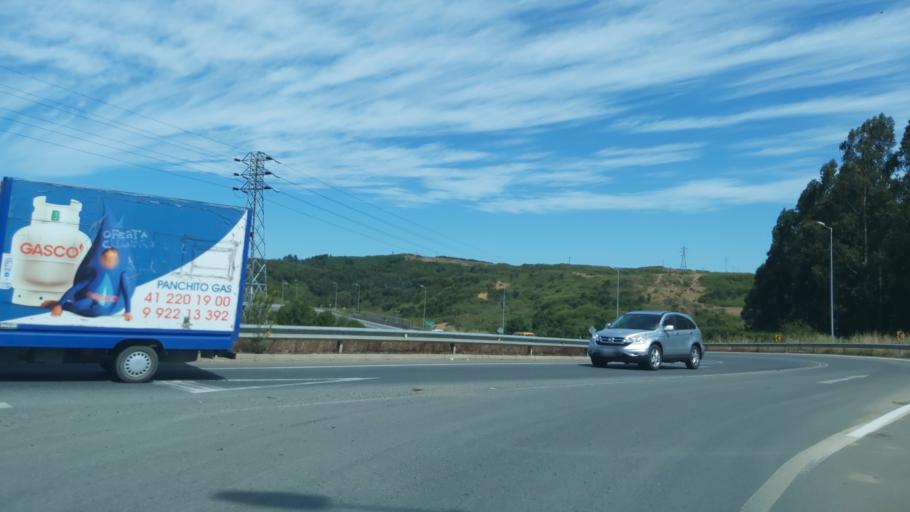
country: CL
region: Biobio
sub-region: Provincia de Concepcion
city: Coronel
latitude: -37.0242
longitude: -73.1333
